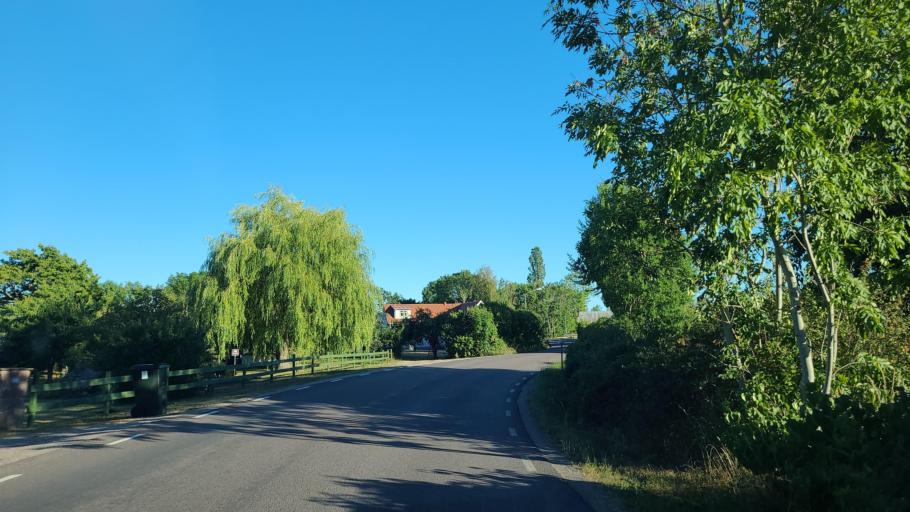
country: SE
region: Kalmar
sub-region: Borgholms Kommun
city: Borgholm
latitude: 57.3199
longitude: 17.0159
